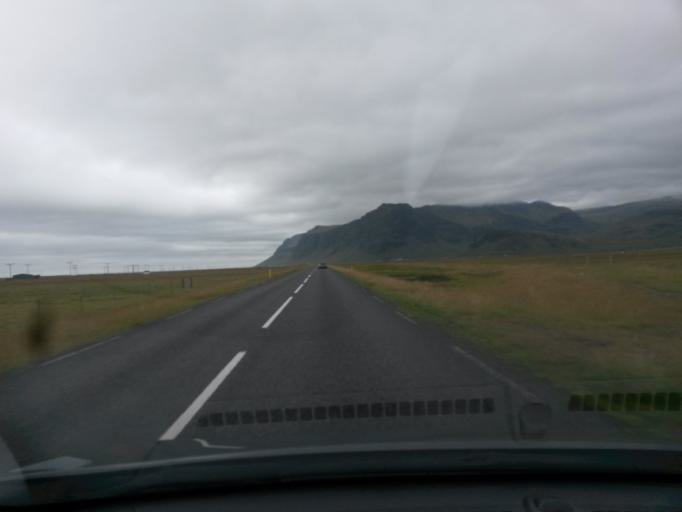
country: IS
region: South
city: Vestmannaeyjar
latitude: 63.5241
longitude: -19.5841
